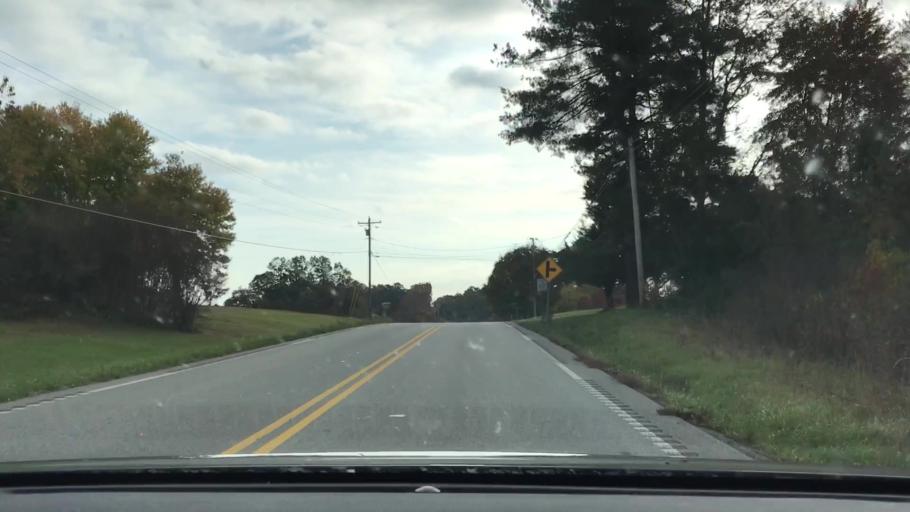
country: US
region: Tennessee
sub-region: Fentress County
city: Jamestown
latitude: 36.3857
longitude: -84.9294
